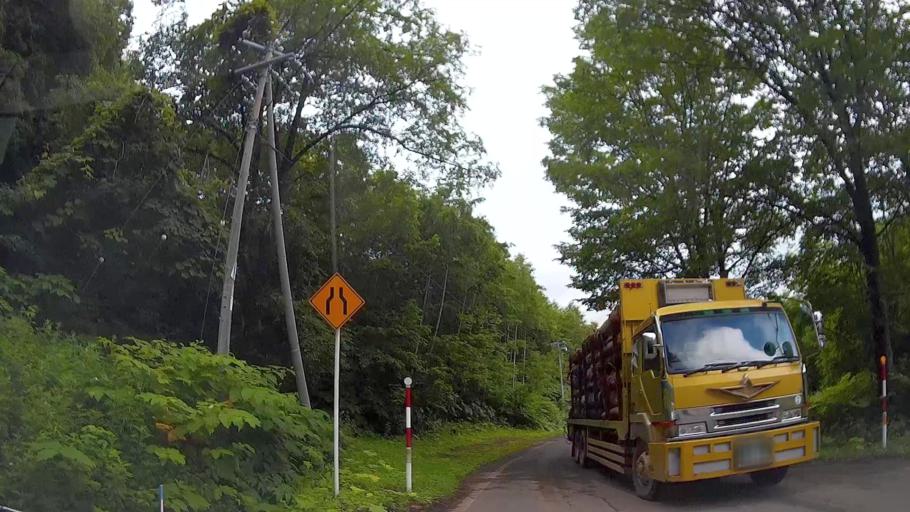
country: JP
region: Hokkaido
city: Nanae
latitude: 42.0723
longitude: 140.5209
